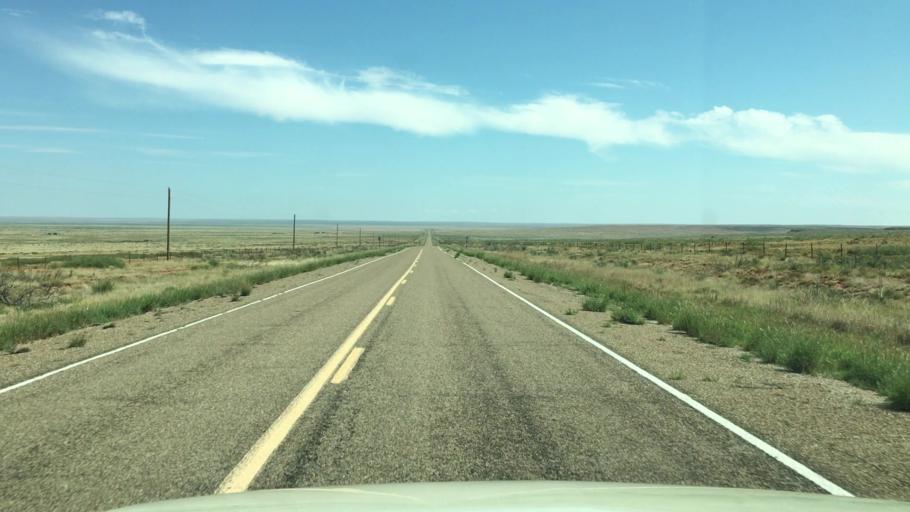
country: US
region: New Mexico
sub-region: Chaves County
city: Roswell
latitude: 33.9780
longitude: -104.5761
